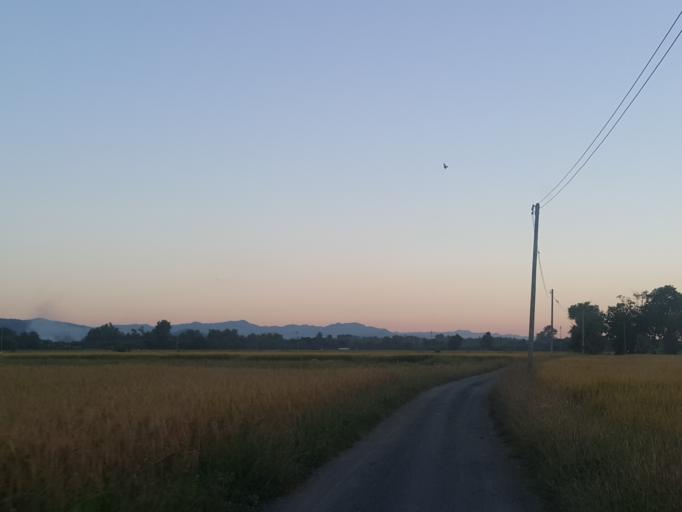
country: TH
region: Chiang Mai
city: San Kamphaeng
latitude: 18.8288
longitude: 99.1532
